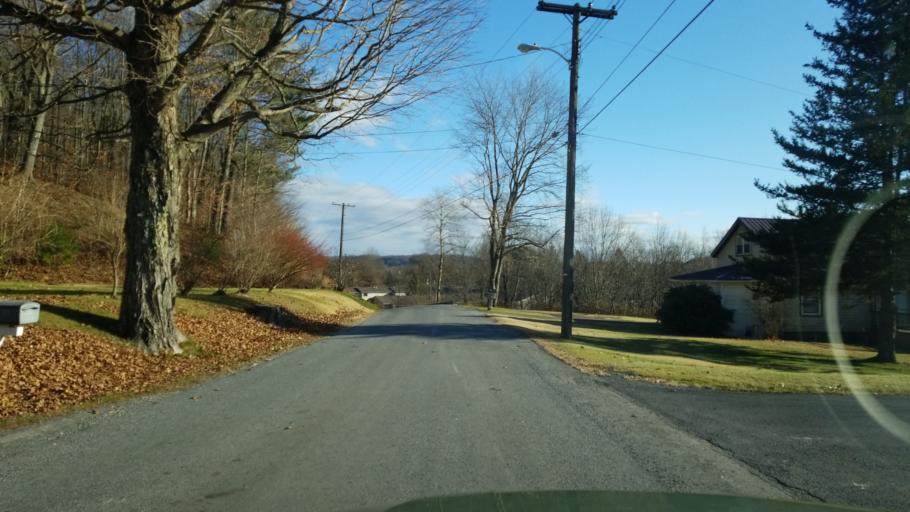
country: US
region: Pennsylvania
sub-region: Jefferson County
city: Brockway
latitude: 41.2546
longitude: -78.7957
